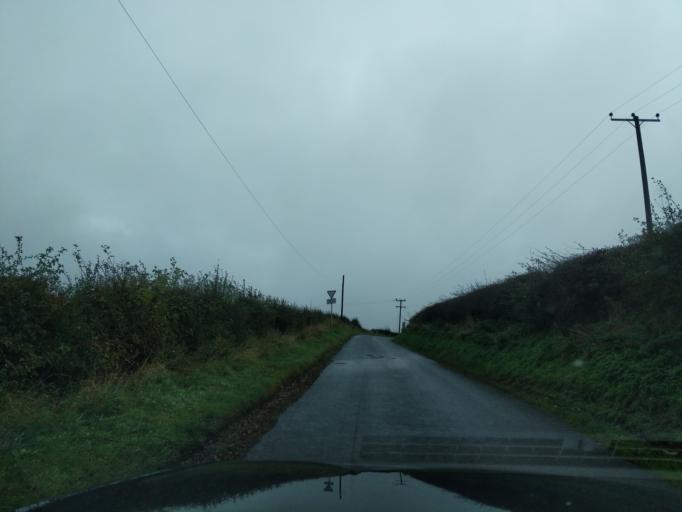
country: GB
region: Scotland
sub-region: East Lothian
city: Dunbar
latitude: 55.9452
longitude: -2.4035
